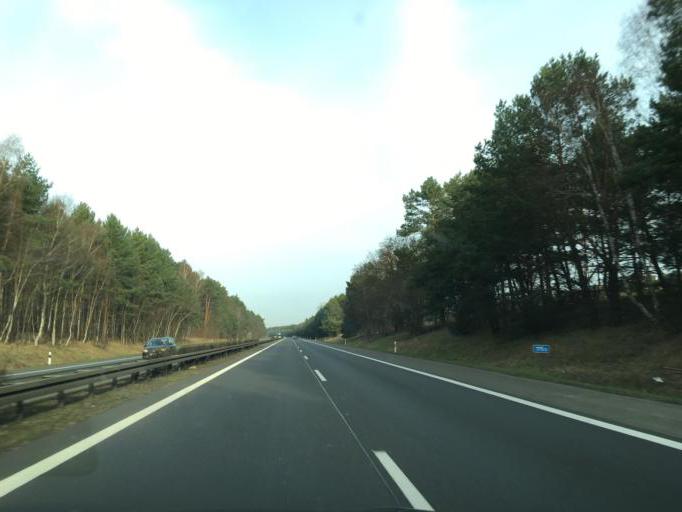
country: DE
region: Brandenburg
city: Birkenwerder
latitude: 52.6930
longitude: 13.3104
